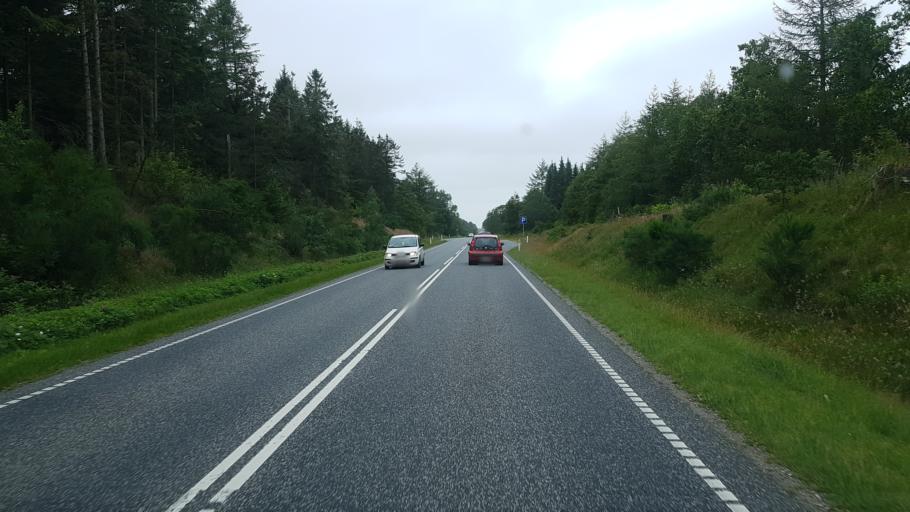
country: DK
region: Central Jutland
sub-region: Lemvig Kommune
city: Lemvig
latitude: 56.4539
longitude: 8.3424
